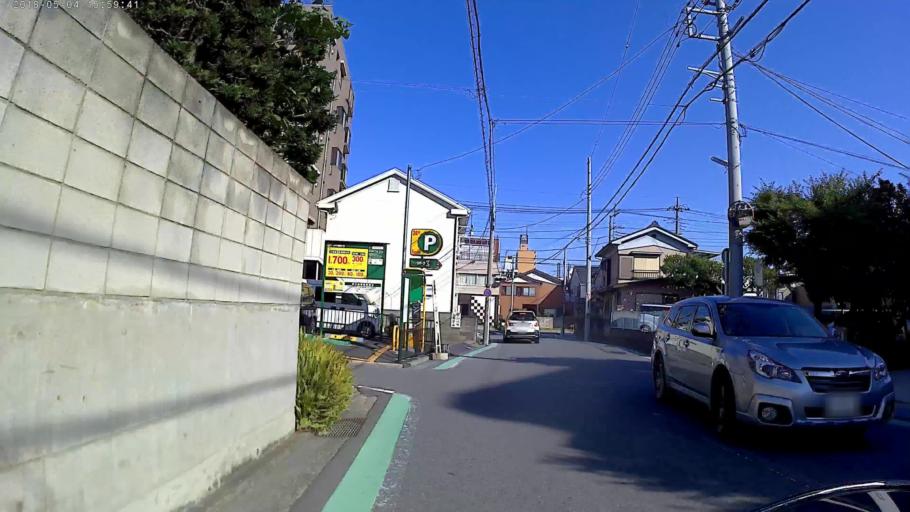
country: JP
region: Kanagawa
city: Yokohama
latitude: 35.4969
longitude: 139.6663
